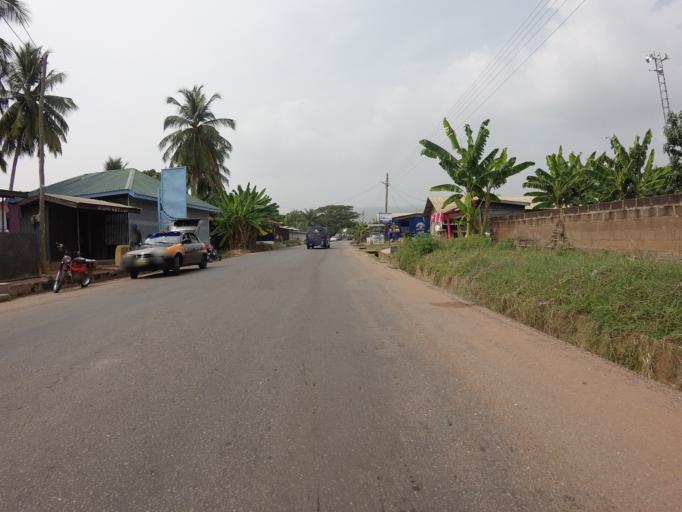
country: GH
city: Akropong
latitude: 6.1030
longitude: -0.0086
